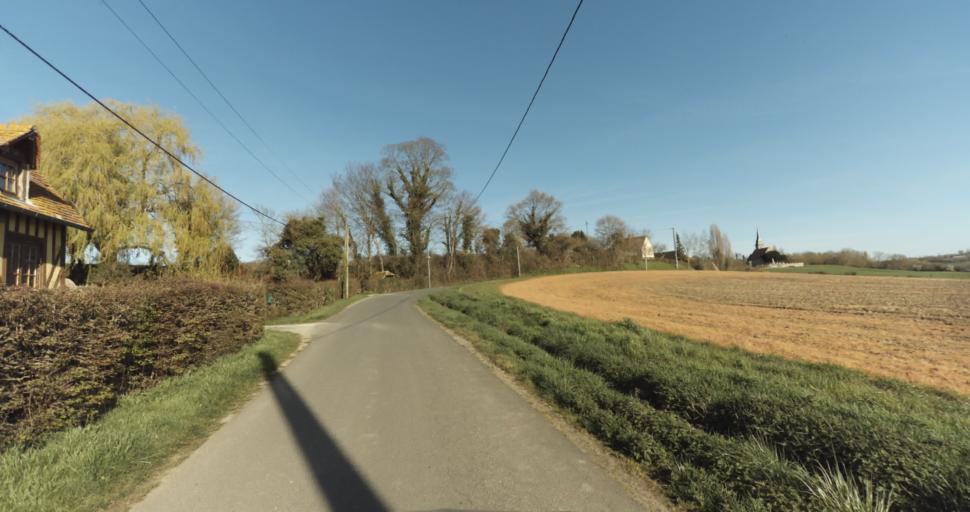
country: FR
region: Lower Normandy
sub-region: Departement du Calvados
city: Saint-Pierre-sur-Dives
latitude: 49.0418
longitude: 0.0343
